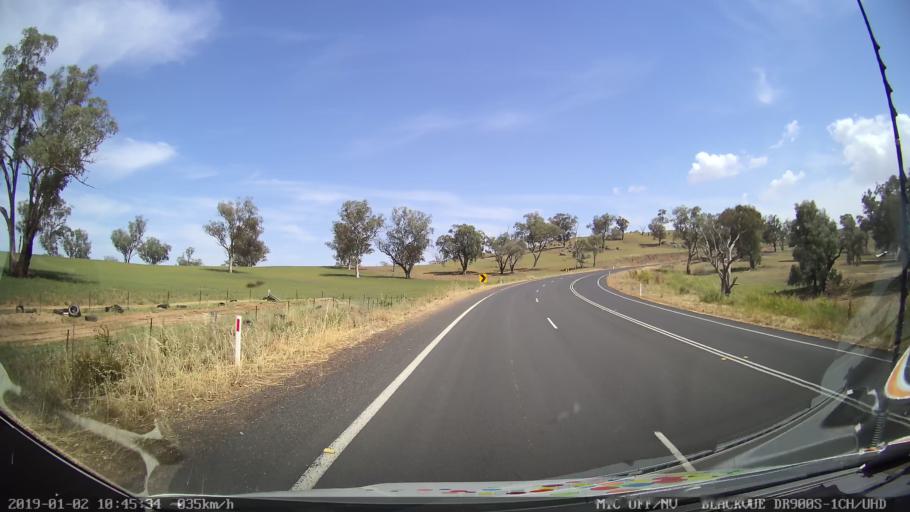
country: AU
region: New South Wales
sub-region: Cootamundra
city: Cootamundra
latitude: -34.7578
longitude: 148.2899
